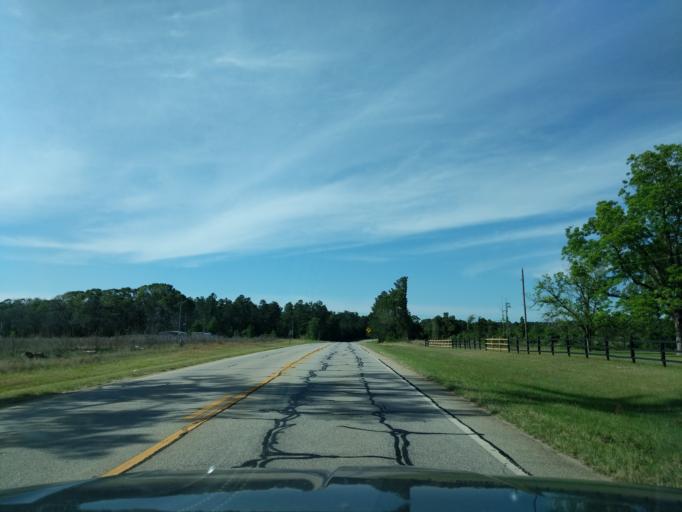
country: US
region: Georgia
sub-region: Jefferson County
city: Wrens
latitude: 33.2513
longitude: -82.3871
